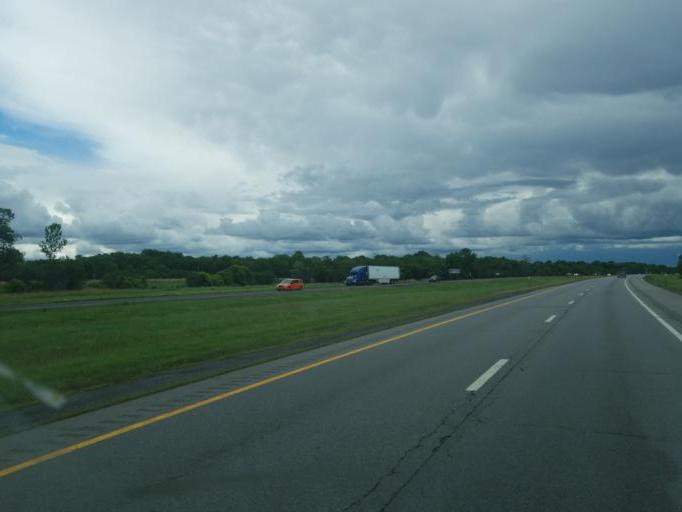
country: US
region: New York
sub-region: Ontario County
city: Phelps
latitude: 42.9740
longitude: -77.0949
